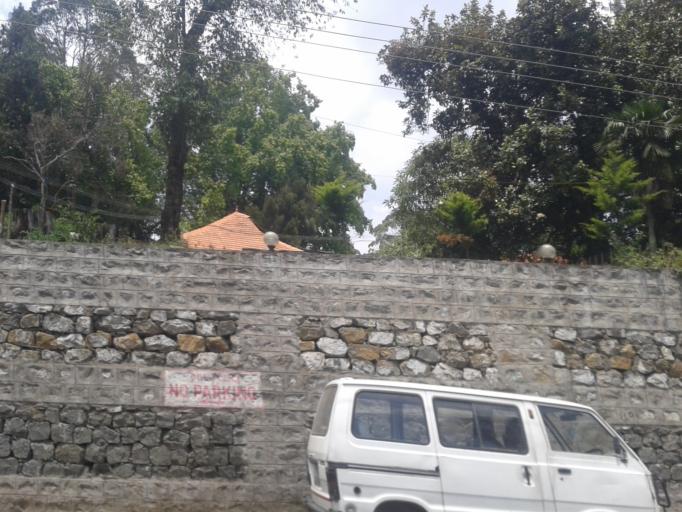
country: IN
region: Tamil Nadu
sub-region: Dindigul
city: Kodaikanal
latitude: 10.2383
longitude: 77.4878
